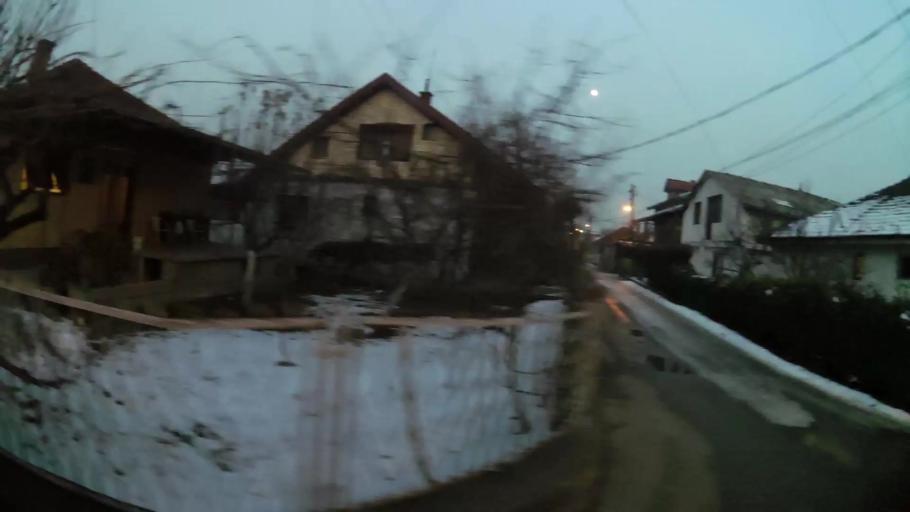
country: MK
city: Creshevo
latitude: 42.0073
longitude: 21.5123
